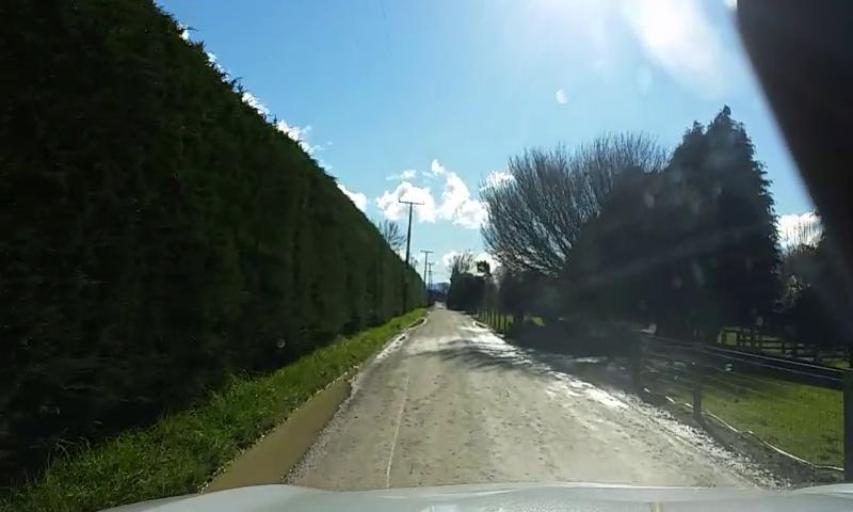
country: NZ
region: Tasman
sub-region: Tasman District
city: Richmond
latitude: -41.3028
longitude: 173.1443
